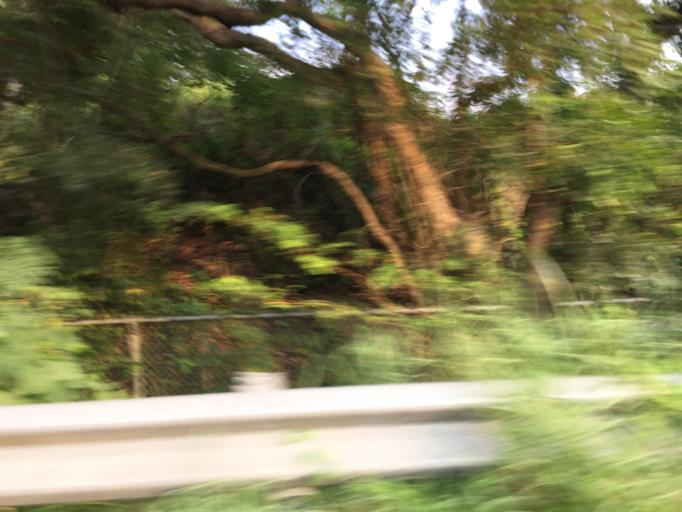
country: TW
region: Taiwan
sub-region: Hsinchu
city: Hsinchu
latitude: 24.7761
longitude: 120.9541
